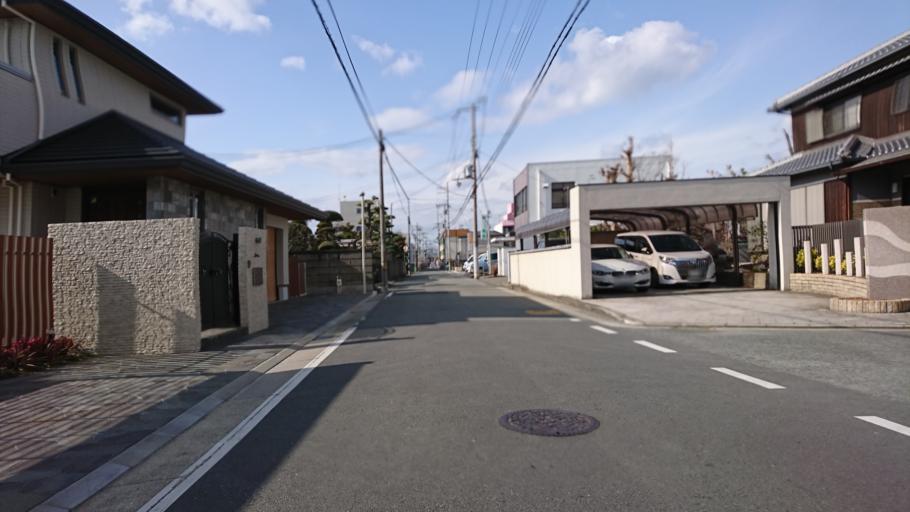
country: JP
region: Hyogo
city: Kakogawacho-honmachi
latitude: 34.7604
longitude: 134.8316
